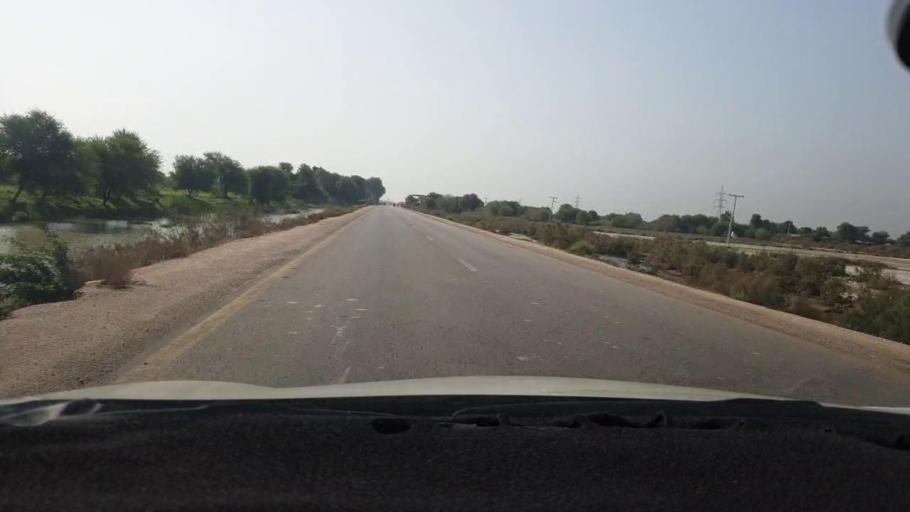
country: PK
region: Sindh
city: Sanghar
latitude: 25.9921
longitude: 68.9650
